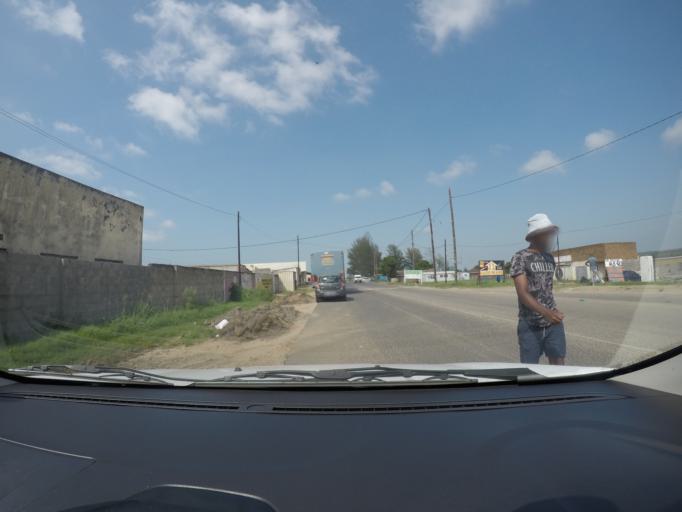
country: ZA
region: KwaZulu-Natal
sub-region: uThungulu District Municipality
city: eSikhawini
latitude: -28.8894
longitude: 31.8945
